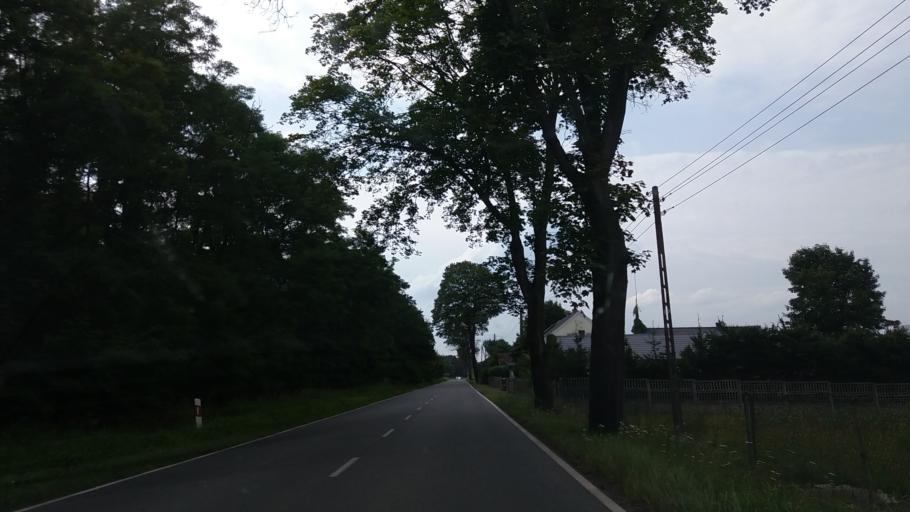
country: PL
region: Lubusz
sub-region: Powiat strzelecko-drezdenecki
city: Zwierzyn
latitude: 52.7248
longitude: 15.5584
